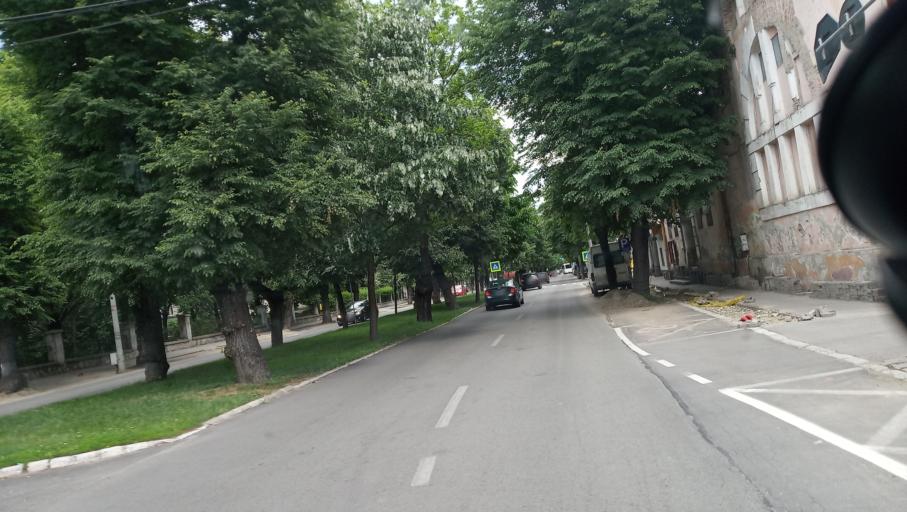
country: RO
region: Bistrita-Nasaud
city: Bistrita
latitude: 47.1338
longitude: 24.4946
